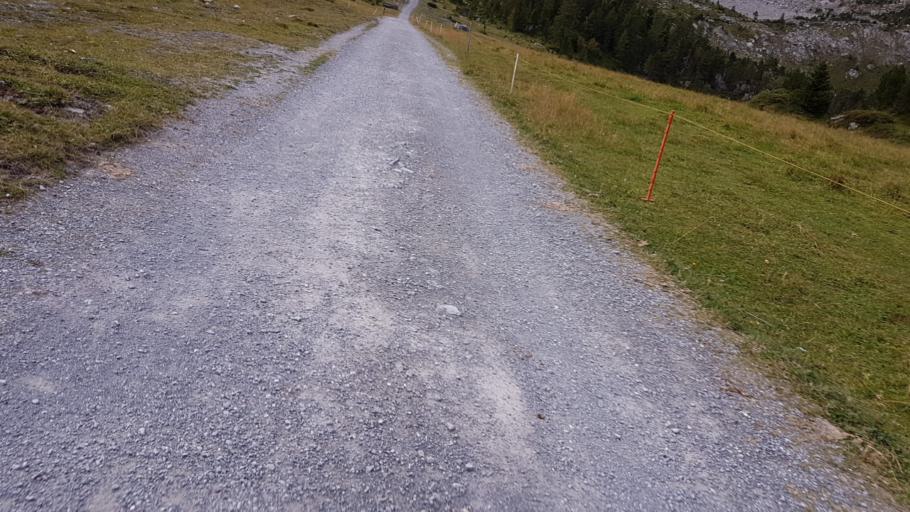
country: CH
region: Valais
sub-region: Leuk District
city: Leukerbad
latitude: 46.4412
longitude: 7.6379
